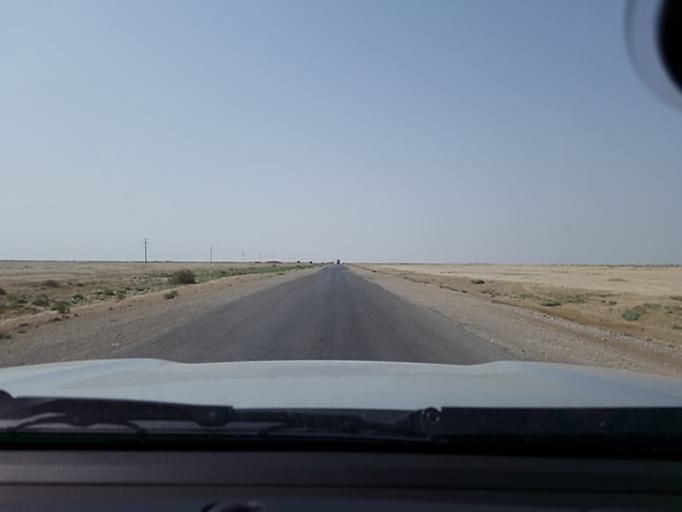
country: TM
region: Balkan
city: Gumdag
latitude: 38.8692
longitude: 54.5942
